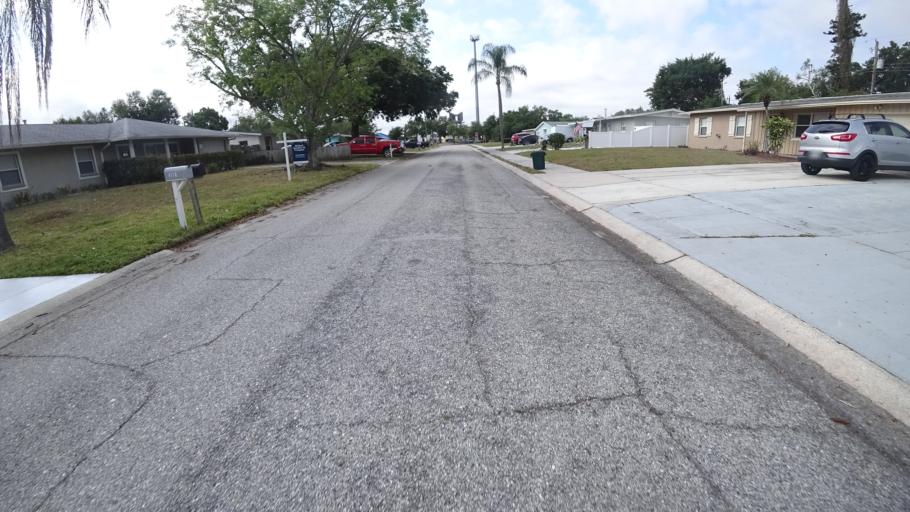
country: US
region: Florida
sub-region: Manatee County
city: South Bradenton
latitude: 27.4646
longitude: -82.6140
